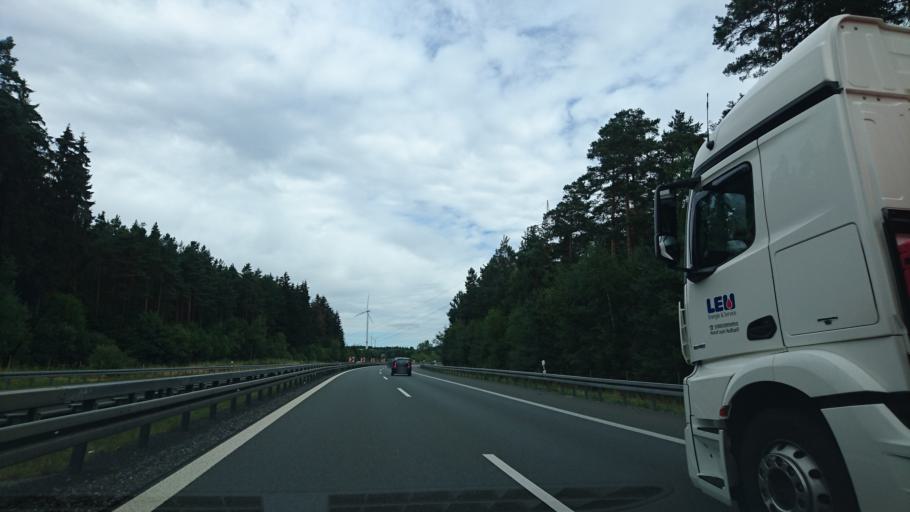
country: DE
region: Bavaria
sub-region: Upper Franconia
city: Thiersheim
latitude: 50.0613
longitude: 12.0987
